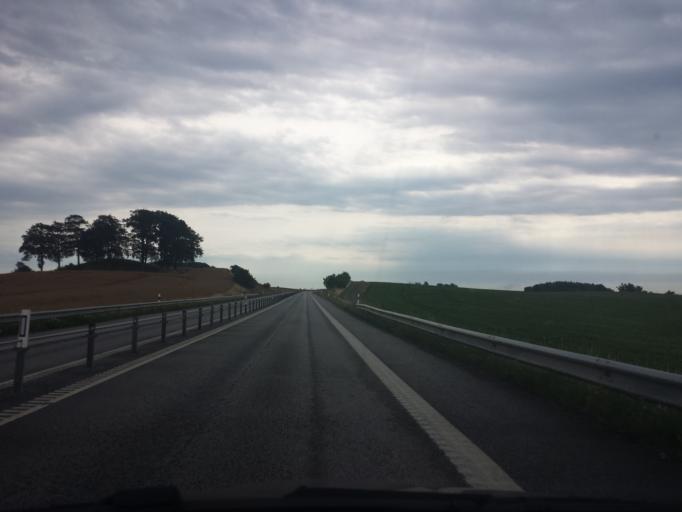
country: SE
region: Skane
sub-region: Ystads Kommun
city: Ystad
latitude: 55.4487
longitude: 13.7686
